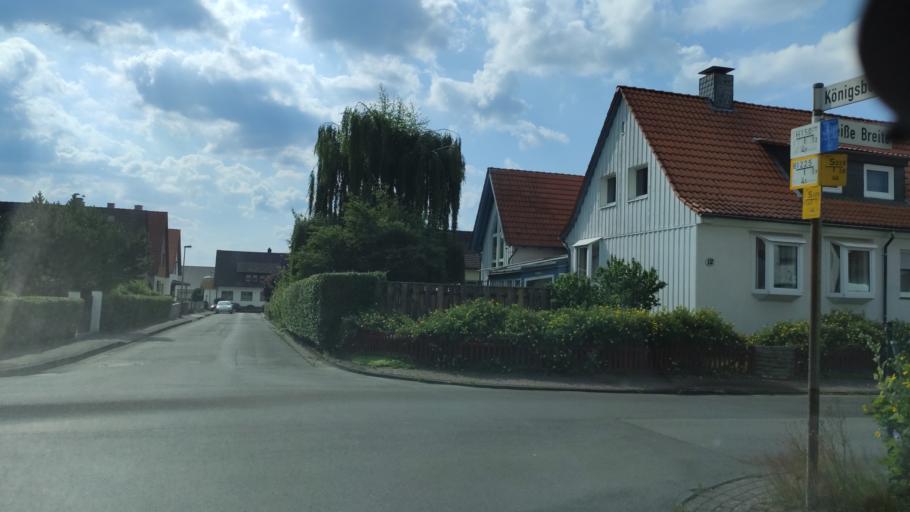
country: DE
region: Lower Saxony
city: Holzminden
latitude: 51.8288
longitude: 9.4724
